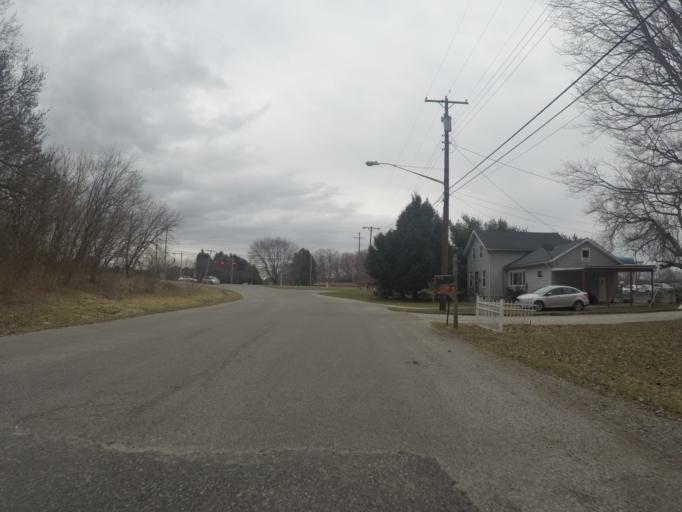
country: US
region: Ohio
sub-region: Portage County
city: Kent
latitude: 41.1577
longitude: -81.3101
